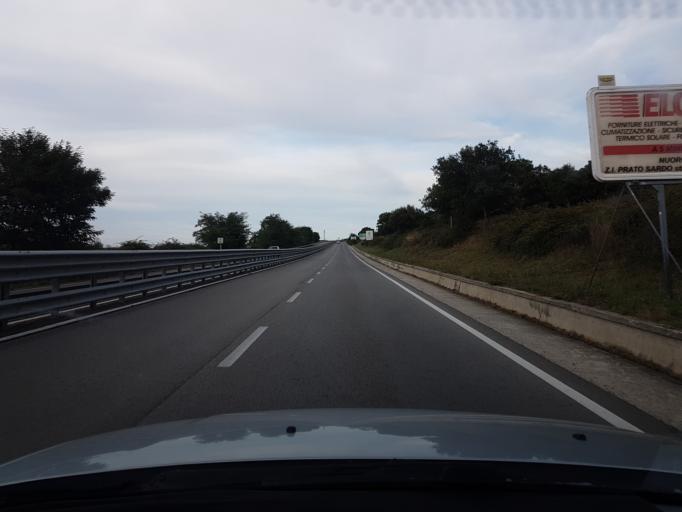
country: IT
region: Sardinia
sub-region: Provincia di Nuoro
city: Nuoro
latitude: 40.3215
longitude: 9.2689
